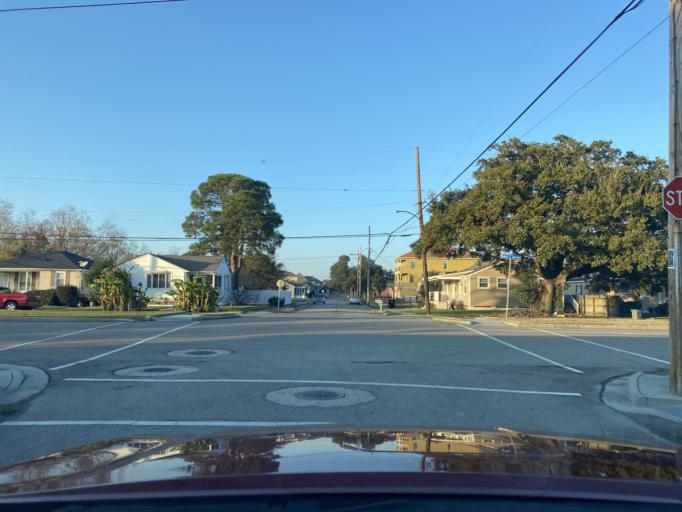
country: US
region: Louisiana
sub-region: Orleans Parish
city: New Orleans
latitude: 30.0220
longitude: -90.0587
